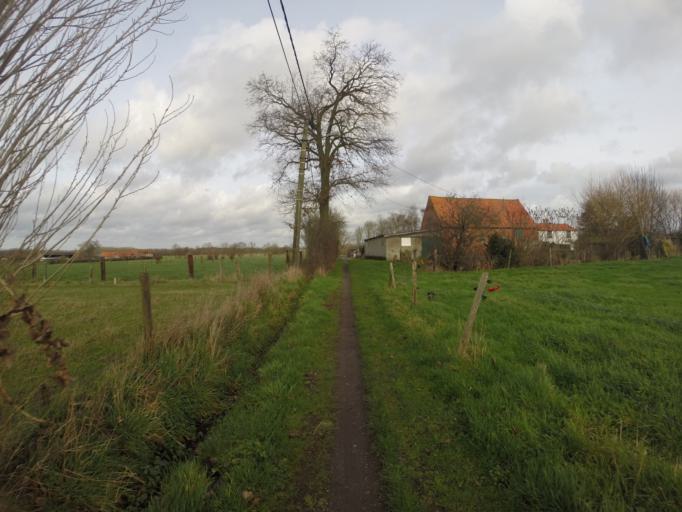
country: BE
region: Flanders
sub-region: Provincie Oost-Vlaanderen
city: Knesselare
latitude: 51.1533
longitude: 3.4262
